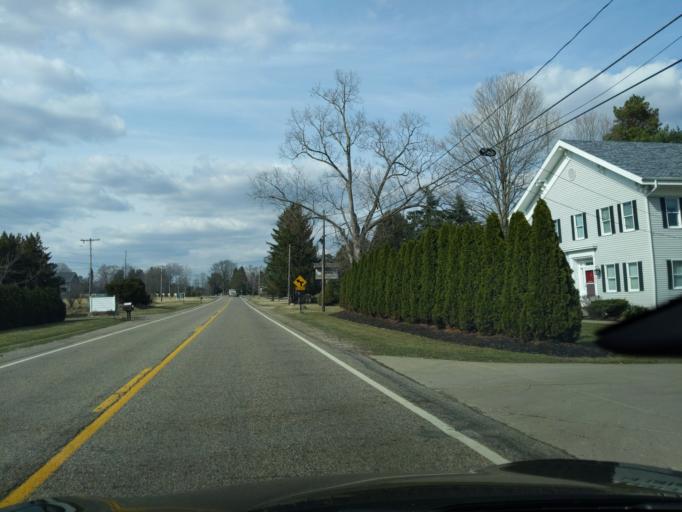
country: US
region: Michigan
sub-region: Jackson County
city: Jackson
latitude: 42.3395
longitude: -84.4135
